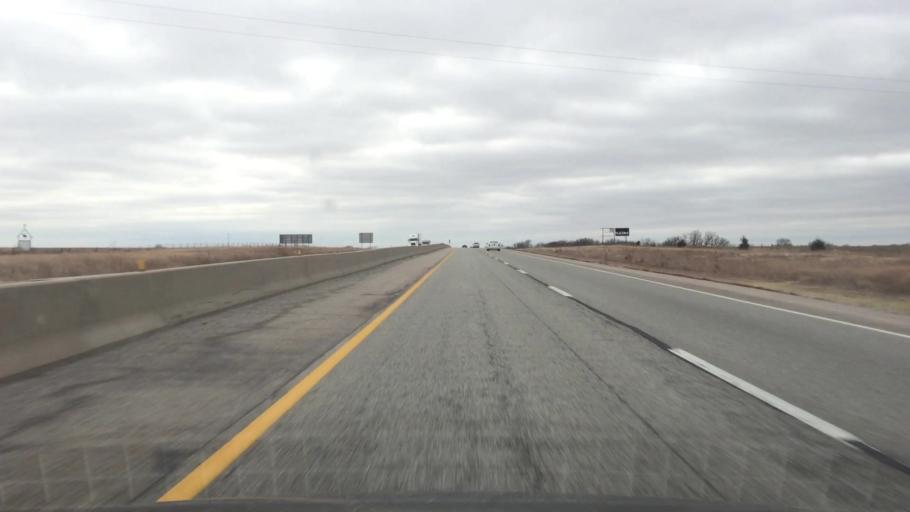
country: US
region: Kansas
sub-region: Butler County
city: El Dorado
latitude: 38.0284
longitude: -96.6602
